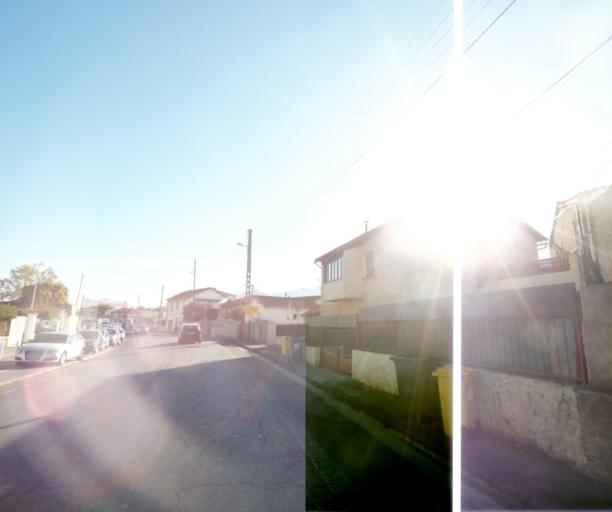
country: FR
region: Provence-Alpes-Cote d'Azur
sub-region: Departement des Bouches-du-Rhone
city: Marseille 11
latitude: 43.2891
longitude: 5.4279
